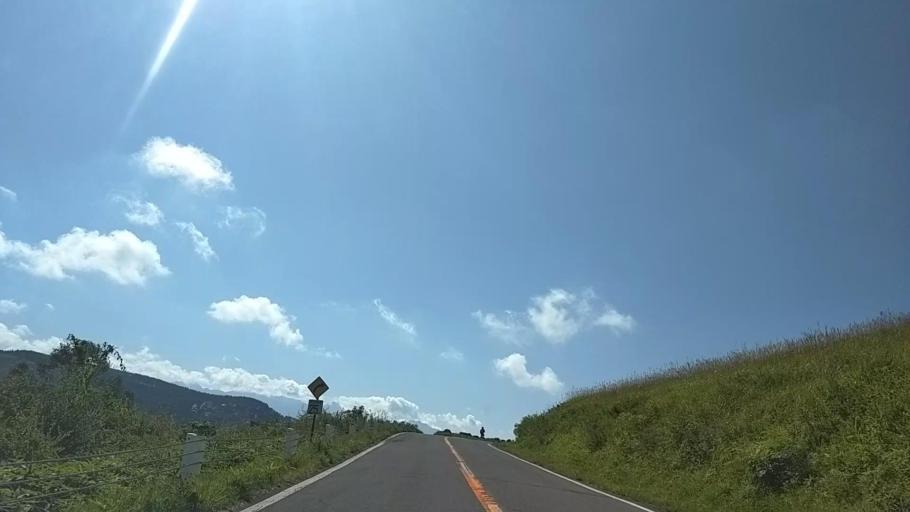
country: JP
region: Nagano
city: Suwa
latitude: 36.0991
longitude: 138.2193
